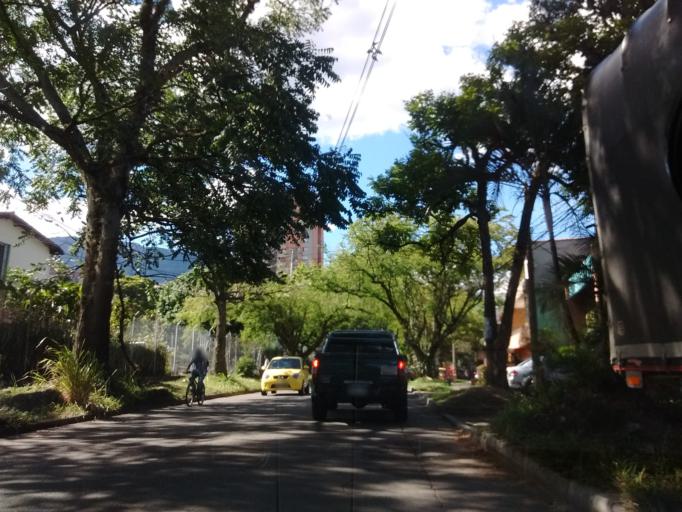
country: CO
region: Antioquia
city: Medellin
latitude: 6.2671
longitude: -75.5972
